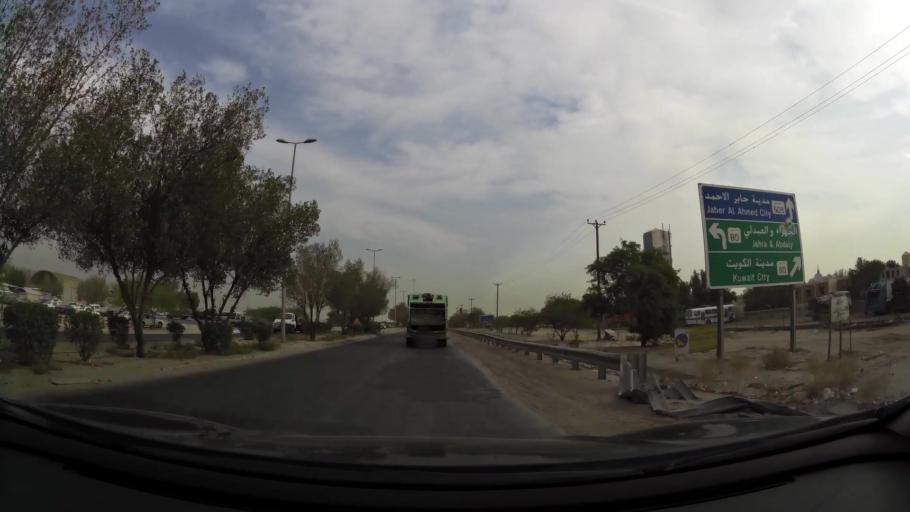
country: KW
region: Muhafazat al Jahra'
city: Al Jahra'
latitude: 29.3191
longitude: 47.7485
